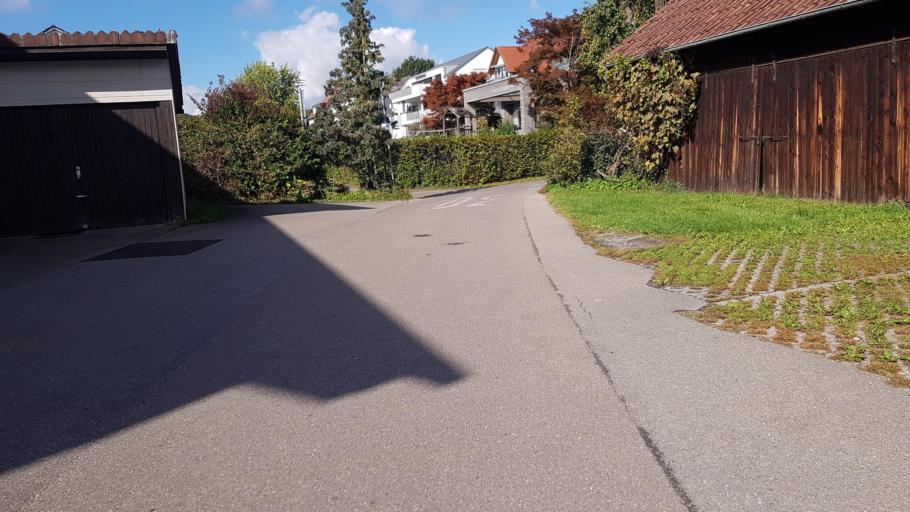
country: DE
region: Baden-Wuerttemberg
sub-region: Tuebingen Region
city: Friedrichshafen
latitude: 47.6581
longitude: 9.4445
